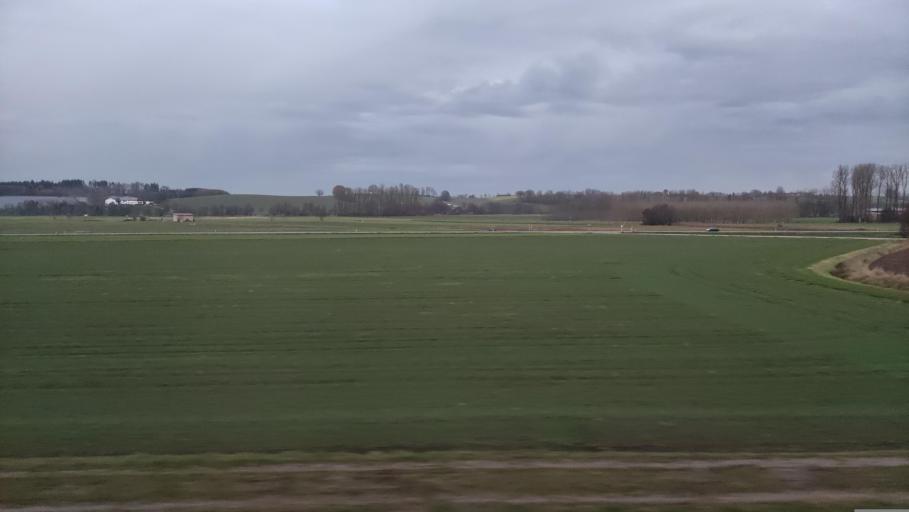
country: DE
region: Bavaria
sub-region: Upper Bavaria
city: Rattenkirchen
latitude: 48.2583
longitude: 12.3386
